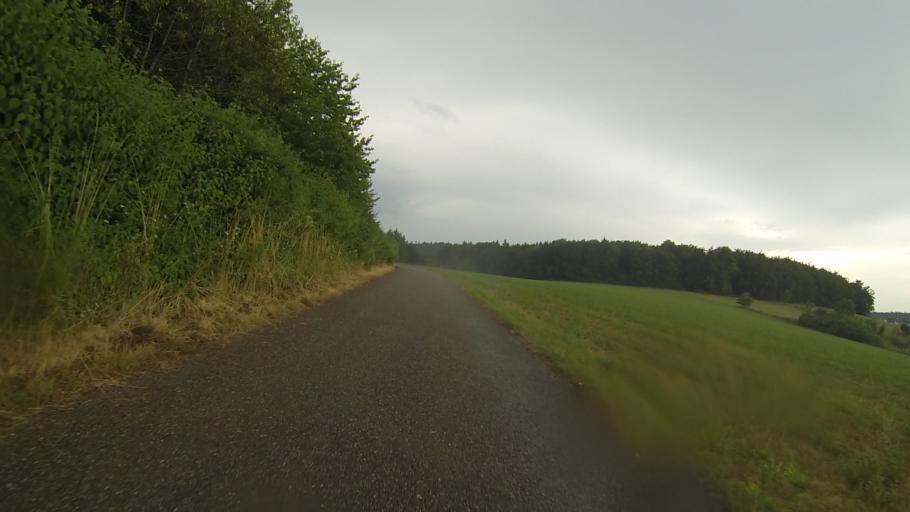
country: DE
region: Baden-Wuerttemberg
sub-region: Regierungsbezirk Stuttgart
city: Heidenheim an der Brenz
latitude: 48.6814
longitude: 10.1783
